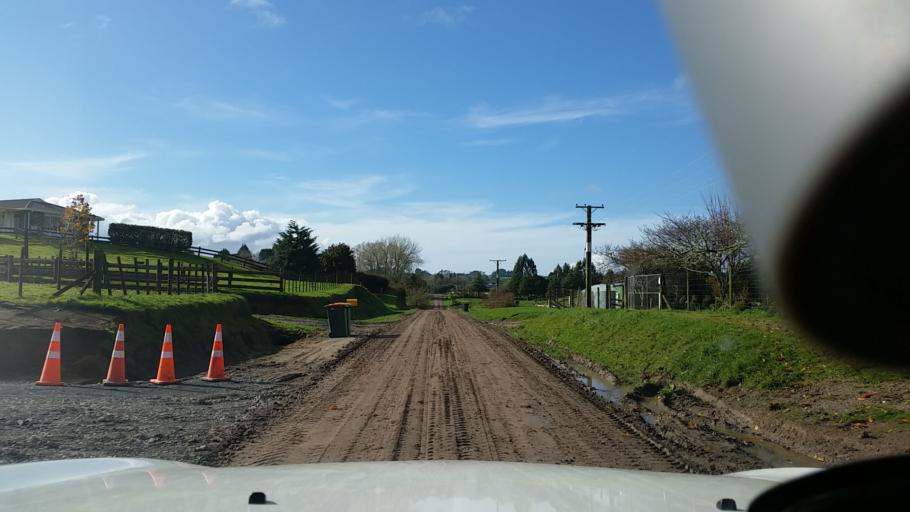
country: NZ
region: Bay of Plenty
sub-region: Rotorua District
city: Rotorua
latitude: -38.0376
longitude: 176.1944
